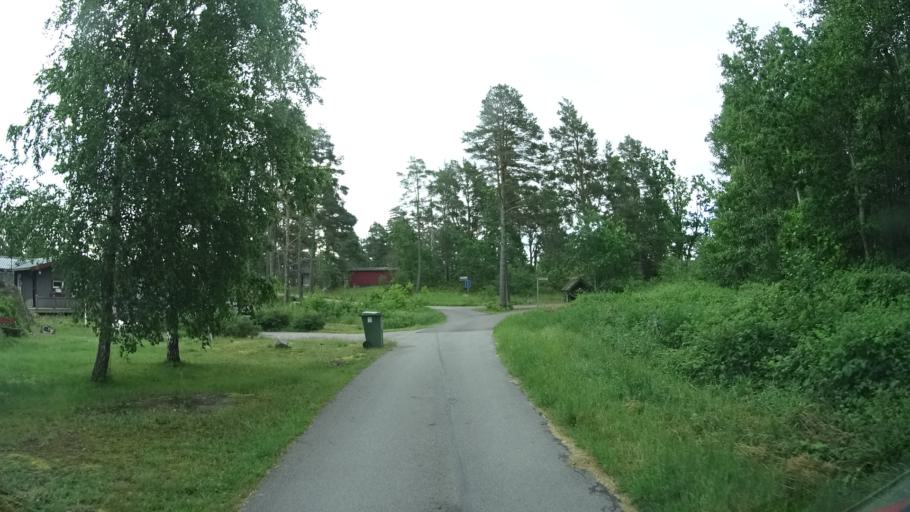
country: SE
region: Kalmar
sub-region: Oskarshamns Kommun
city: Oskarshamn
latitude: 57.2354
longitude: 16.5008
